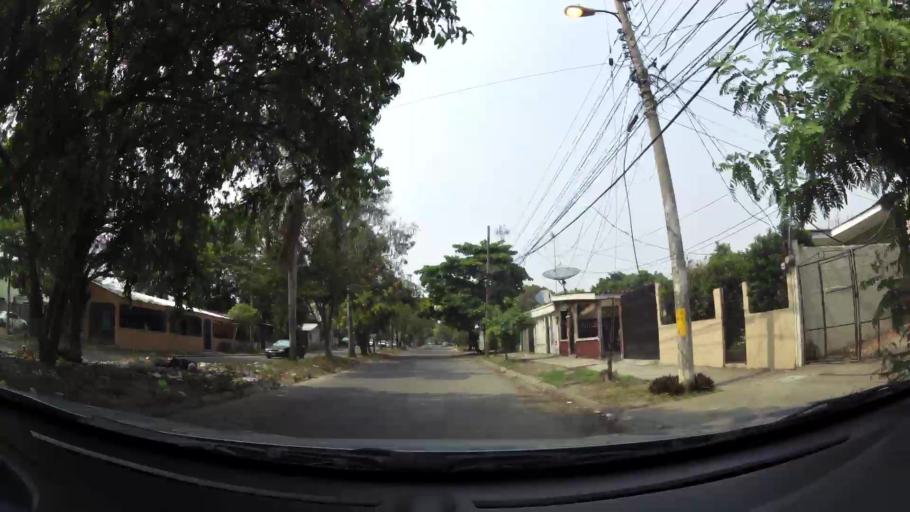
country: HN
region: Cortes
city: San Pedro Sula
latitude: 15.4846
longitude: -88.0168
